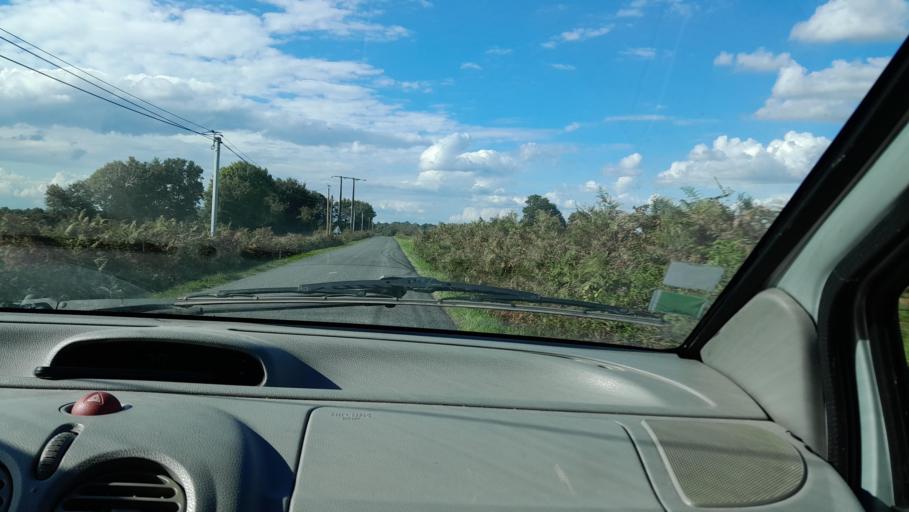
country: FR
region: Pays de la Loire
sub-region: Departement de la Mayenne
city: Ahuille
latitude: 48.0284
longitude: -0.8893
